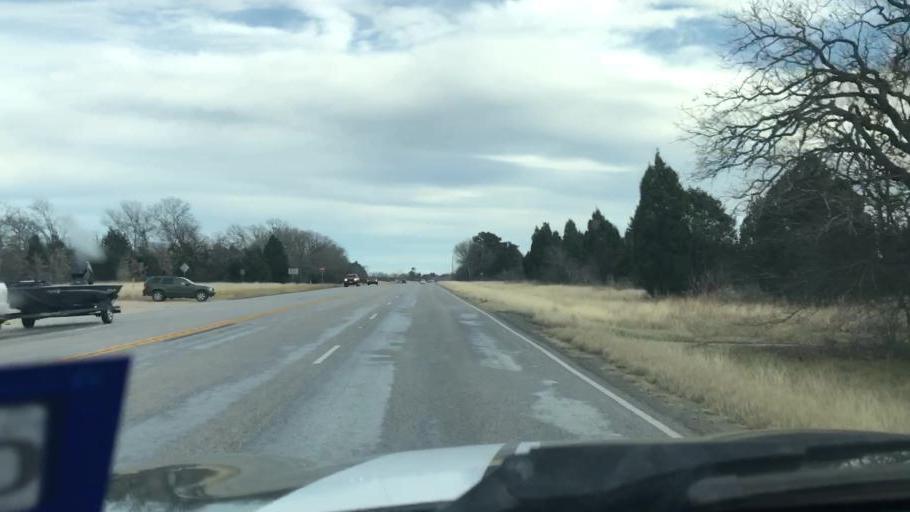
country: US
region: Texas
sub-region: Bastrop County
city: Camp Swift
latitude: 30.2967
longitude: -97.2744
